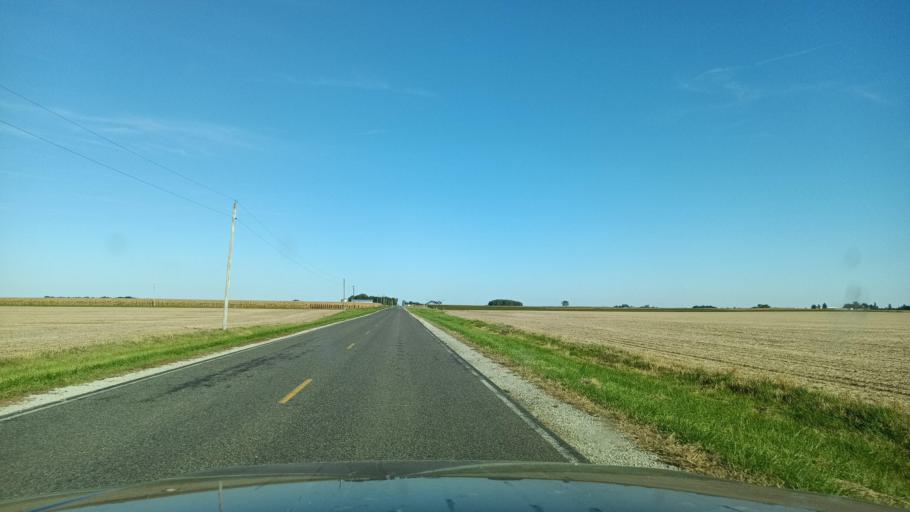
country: US
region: Illinois
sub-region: De Witt County
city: Clinton
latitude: 40.2243
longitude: -88.9311
